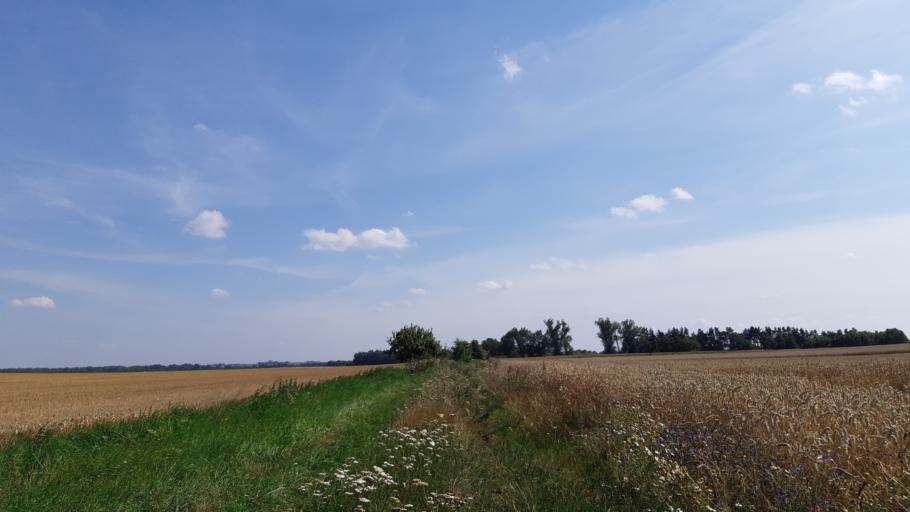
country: LT
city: Virbalis
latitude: 54.6433
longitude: 22.8180
